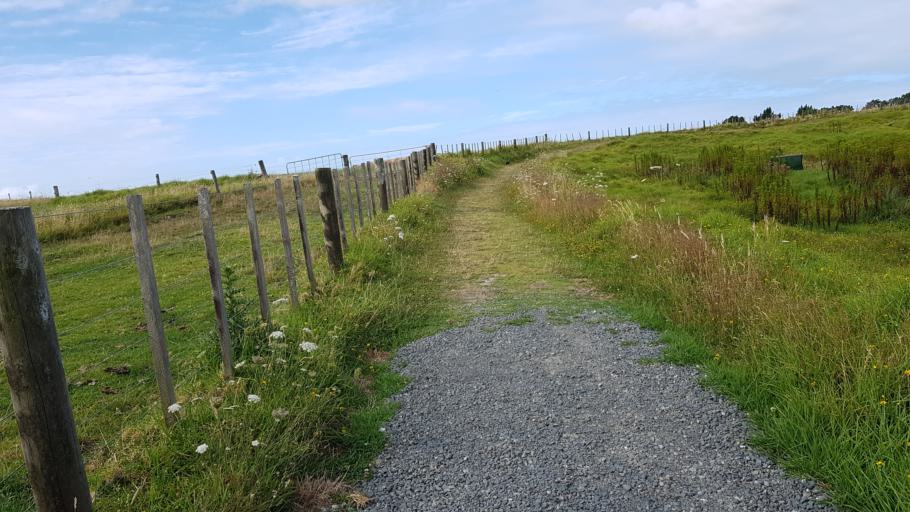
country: NZ
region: Auckland
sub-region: Auckland
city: Rothesay Bay
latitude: -36.6655
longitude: 174.7457
